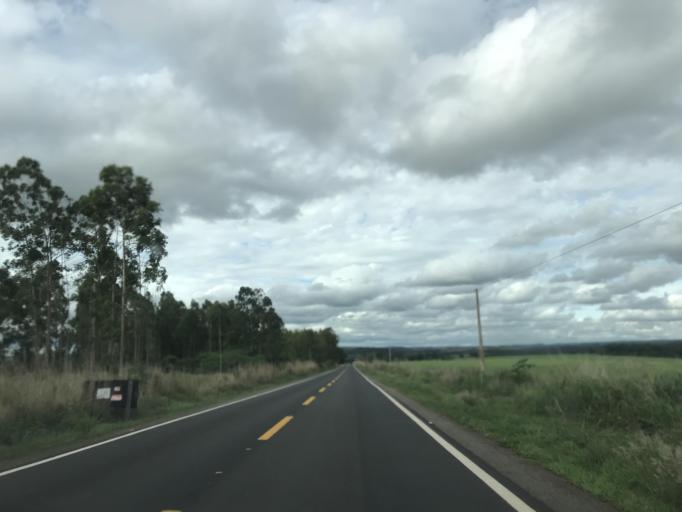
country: BR
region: Goias
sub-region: Bela Vista De Goias
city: Bela Vista de Goias
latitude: -17.1850
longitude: -48.6909
